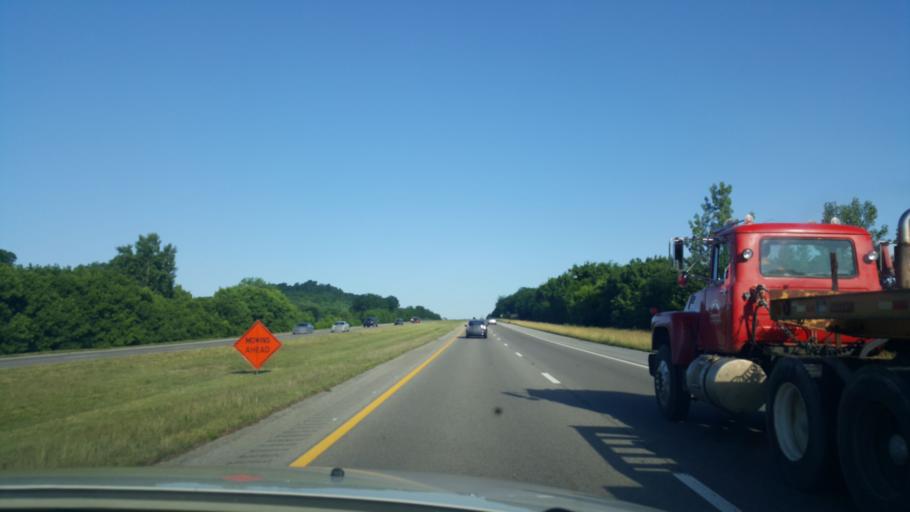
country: US
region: Tennessee
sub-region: Maury County
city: Columbia
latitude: 35.6281
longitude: -87.0870
